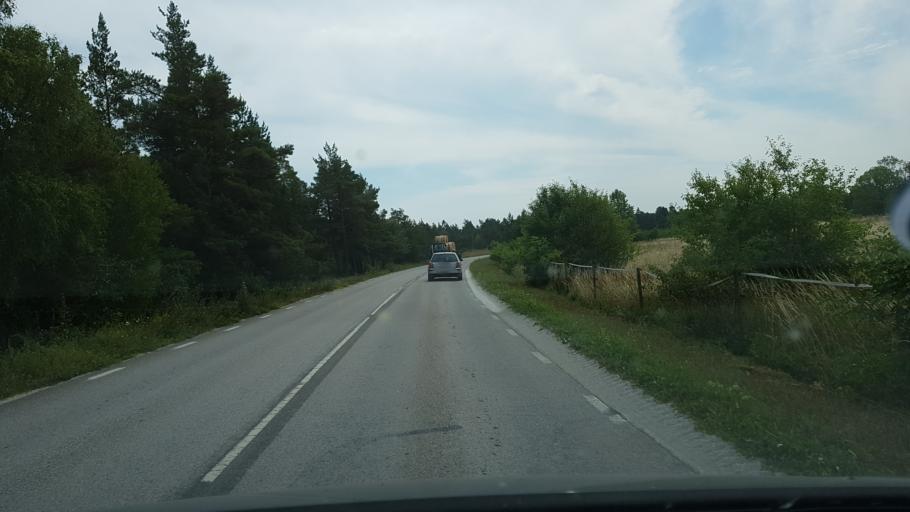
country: SE
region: Gotland
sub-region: Gotland
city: Slite
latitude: 57.7408
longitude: 18.7384
